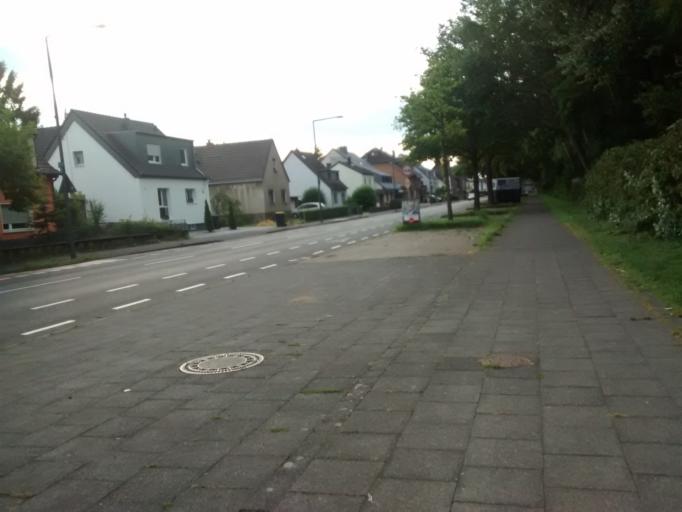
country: DE
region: North Rhine-Westphalia
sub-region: Regierungsbezirk Koln
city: Merheim
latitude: 50.9800
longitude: 7.0480
